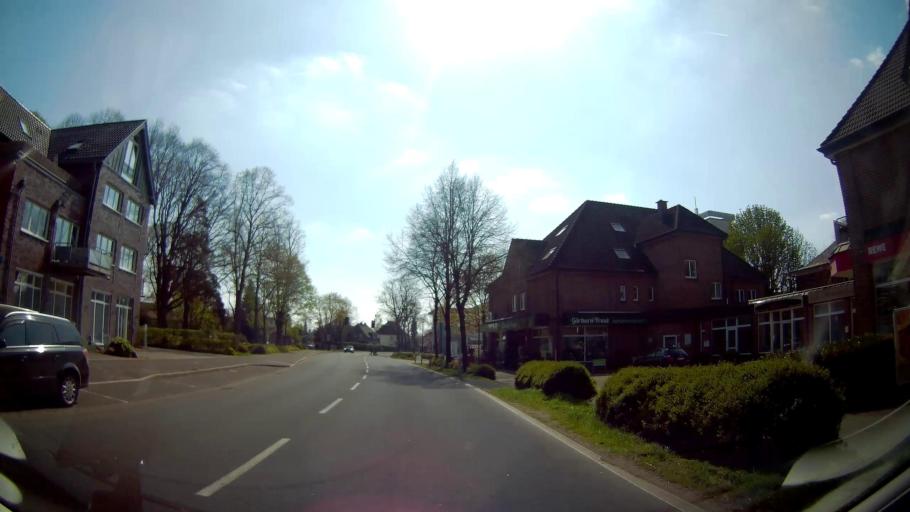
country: DE
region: North Rhine-Westphalia
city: Dorsten
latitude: 51.7174
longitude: 7.0127
